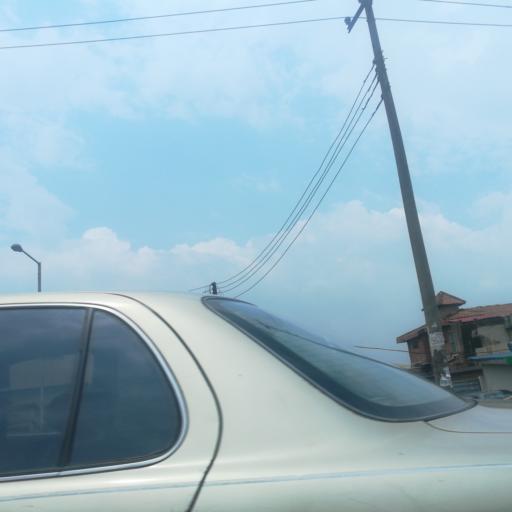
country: NG
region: Lagos
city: Ojota
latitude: 6.5743
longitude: 3.3985
